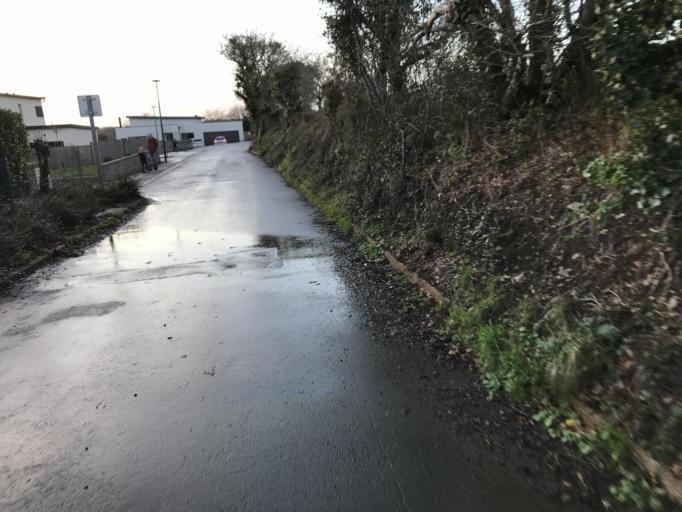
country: FR
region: Brittany
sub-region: Departement du Finistere
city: Hopital-Camfrout
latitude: 48.3349
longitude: -4.2505
